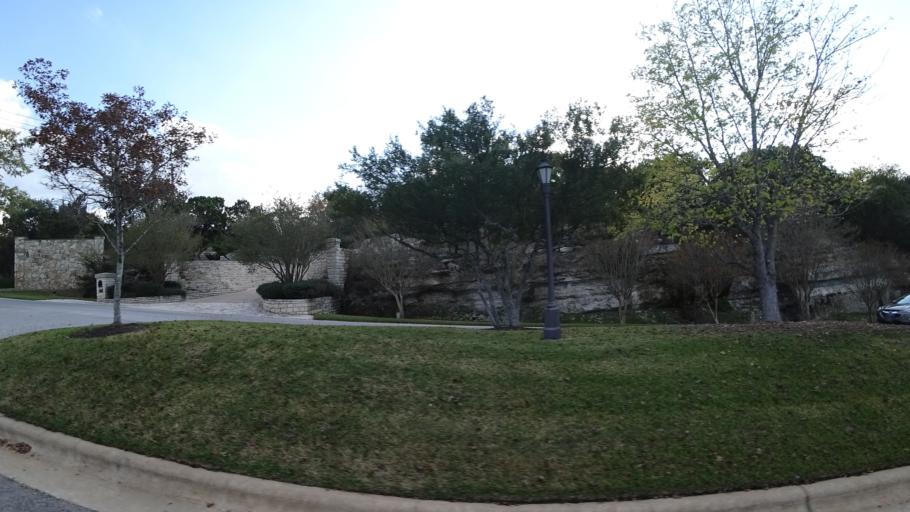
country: US
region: Texas
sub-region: Travis County
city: Barton Creek
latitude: 30.2761
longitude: -97.8646
